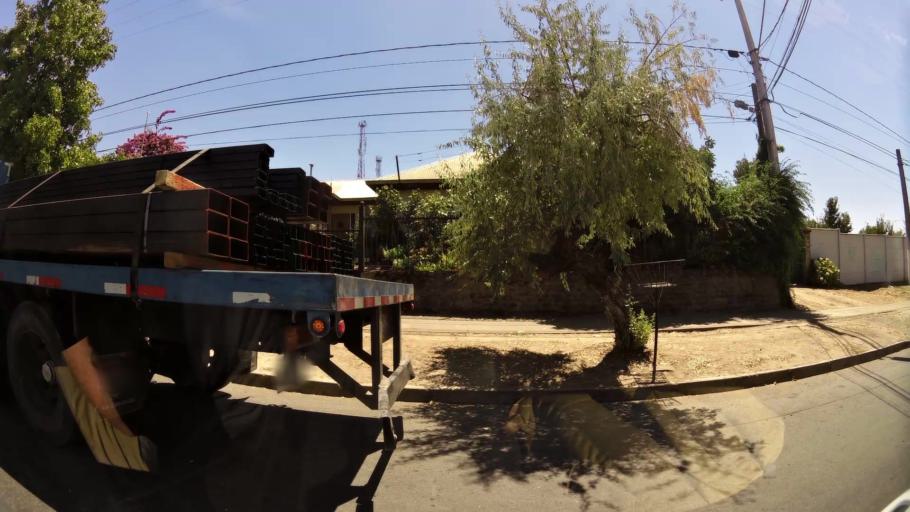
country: CL
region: Maule
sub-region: Provincia de Talca
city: Talca
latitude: -35.3051
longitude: -71.5168
